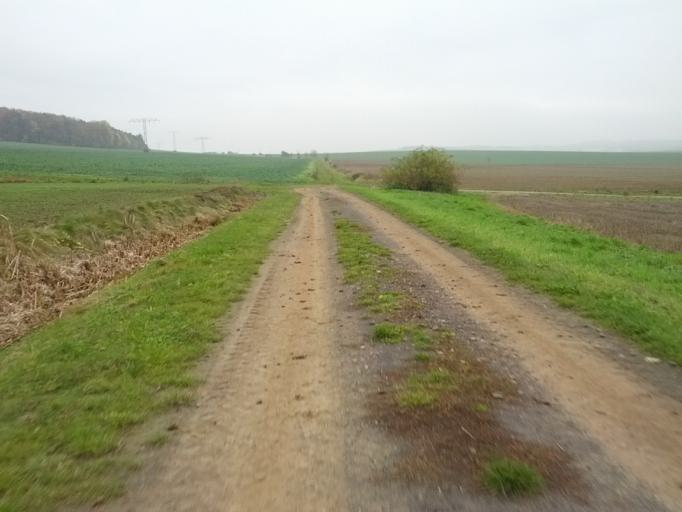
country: DE
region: Thuringia
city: Seebach
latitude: 50.9718
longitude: 10.4269
